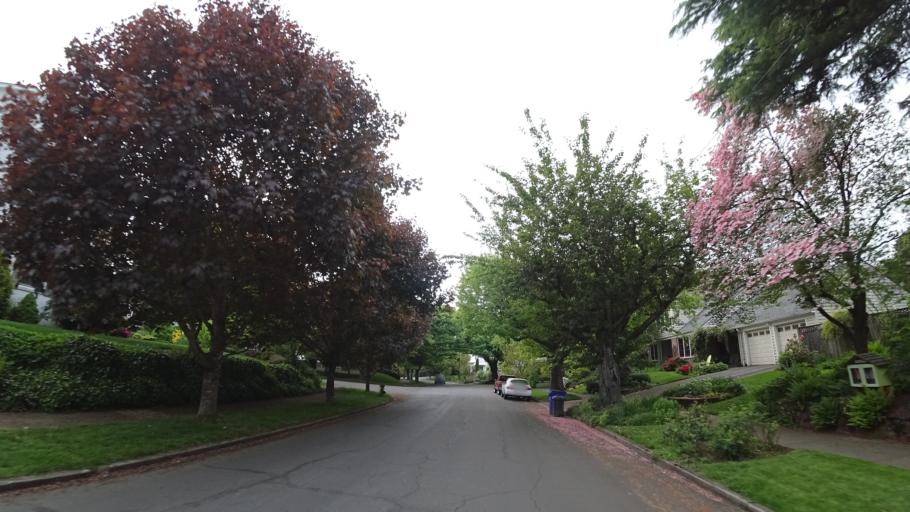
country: US
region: Oregon
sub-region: Clackamas County
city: Milwaukie
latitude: 45.4716
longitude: -122.6307
